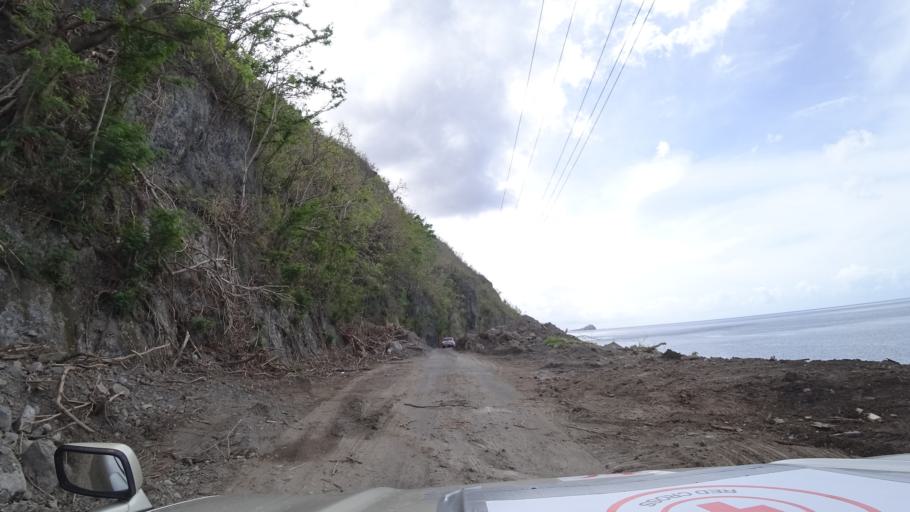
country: DM
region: Saint Luke
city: Pointe Michel
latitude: 15.2560
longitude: -61.3761
